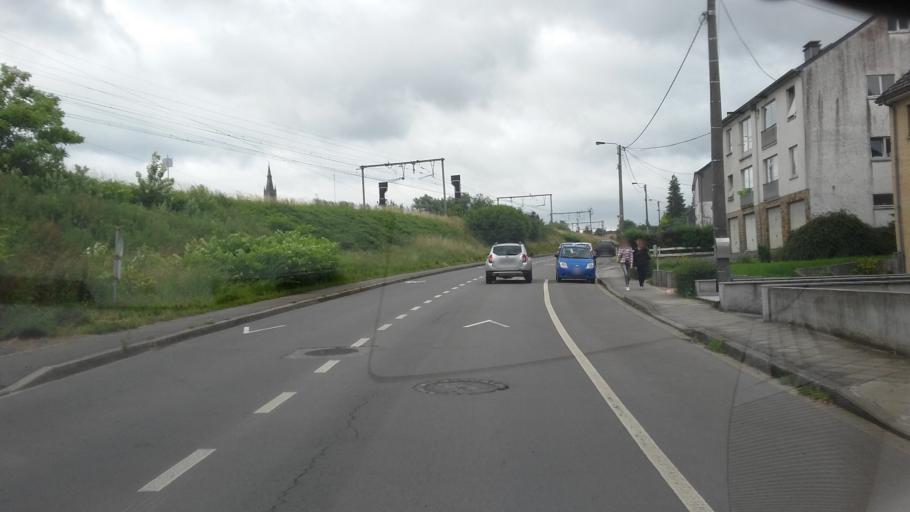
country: BE
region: Wallonia
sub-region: Province du Luxembourg
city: Arlon
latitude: 49.6840
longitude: 5.7976
